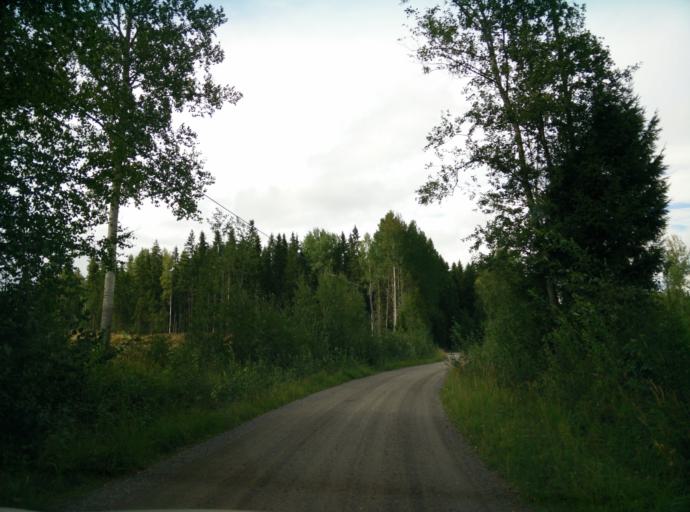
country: FI
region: Haeme
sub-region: Haemeenlinna
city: Kalvola
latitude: 61.1238
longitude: 24.1402
